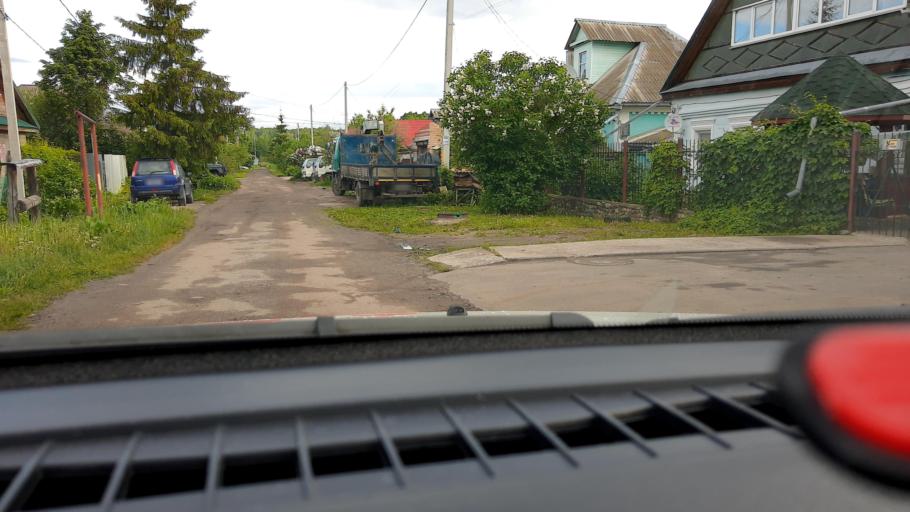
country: RU
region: Nizjnij Novgorod
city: Burevestnik
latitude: 56.2113
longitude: 43.8149
